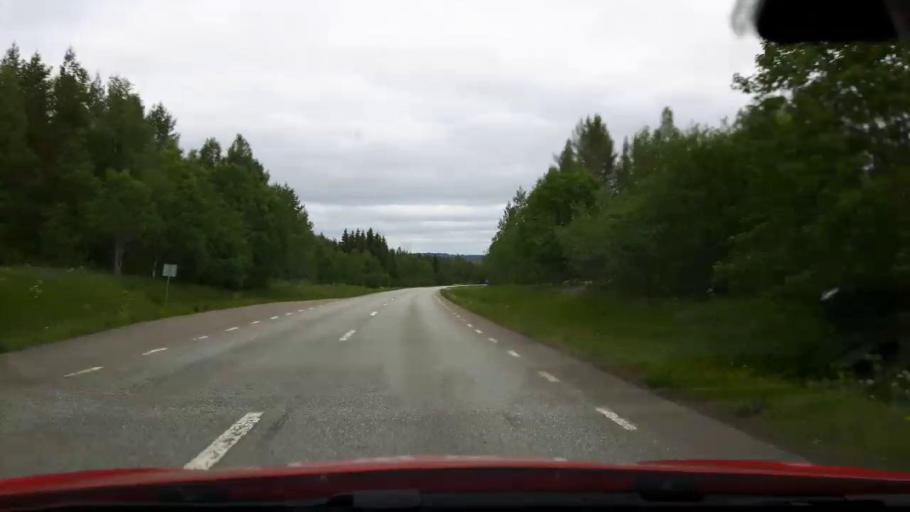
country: SE
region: Jaemtland
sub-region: Krokoms Kommun
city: Krokom
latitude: 63.5875
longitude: 14.6374
